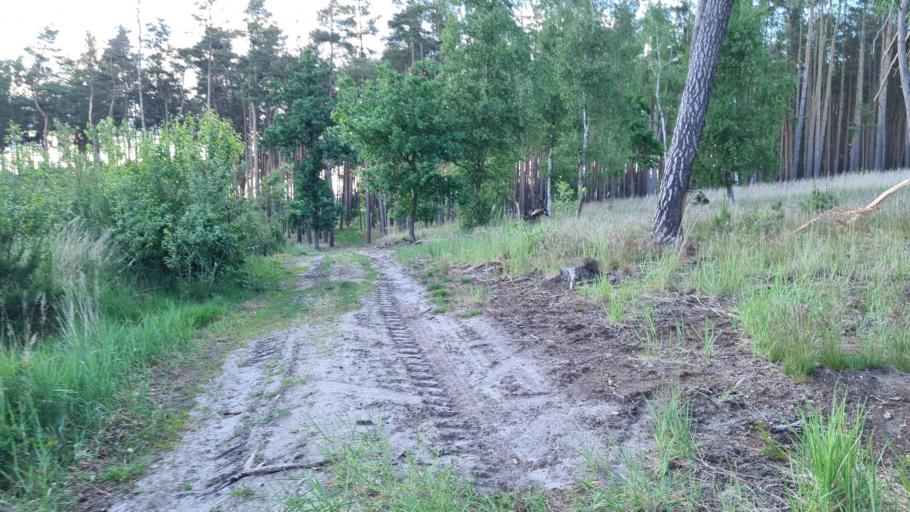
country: DE
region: Brandenburg
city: Schilda
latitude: 51.6062
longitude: 13.3558
